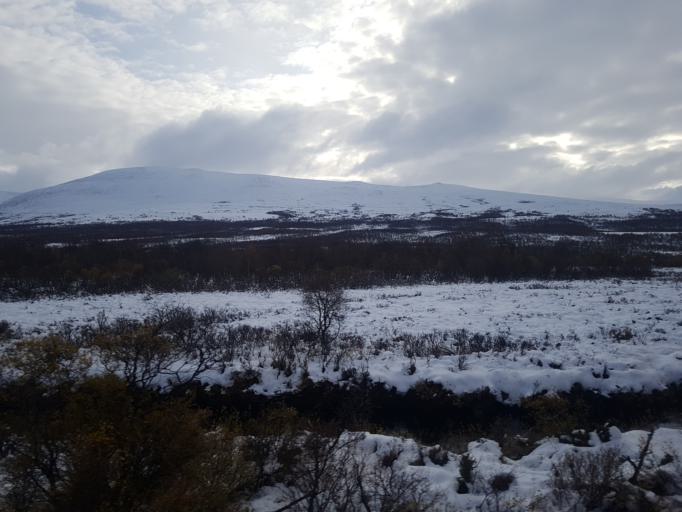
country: NO
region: Oppland
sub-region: Dovre
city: Dovre
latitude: 62.1238
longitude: 9.3010
